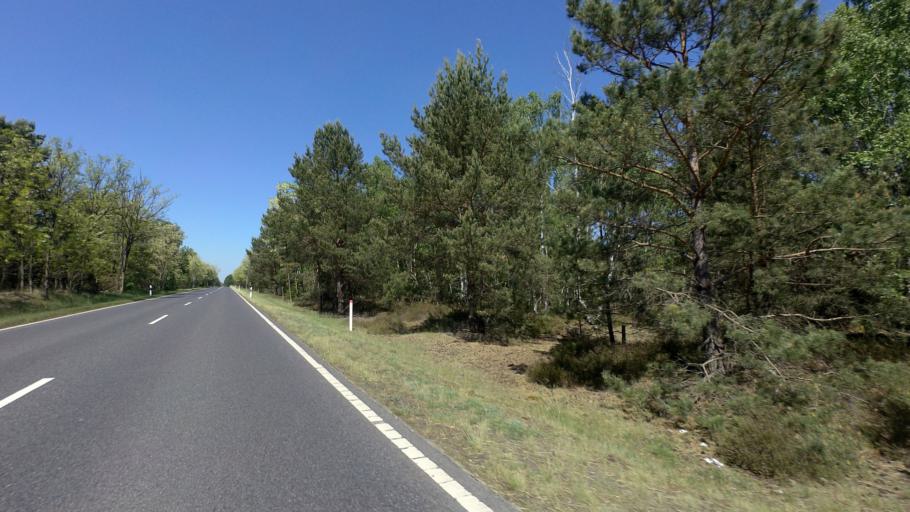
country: DE
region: Brandenburg
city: Drachhausen
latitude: 51.9473
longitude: 14.3354
